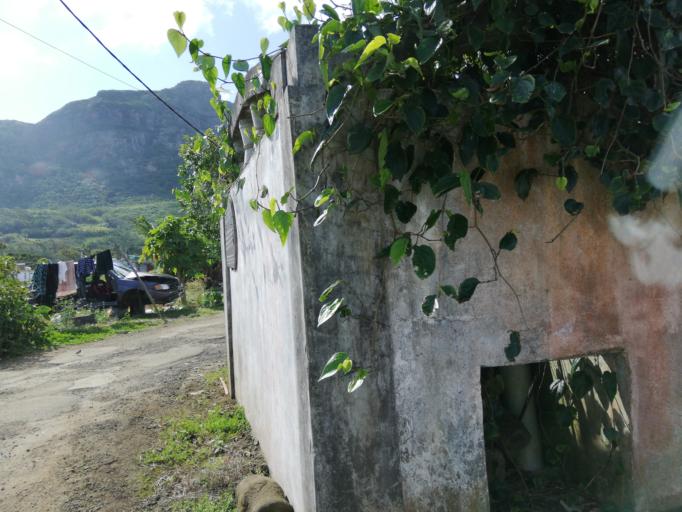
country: MU
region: Pamplemousses
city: Creve Coeur
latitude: -20.2031
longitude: 57.5546
